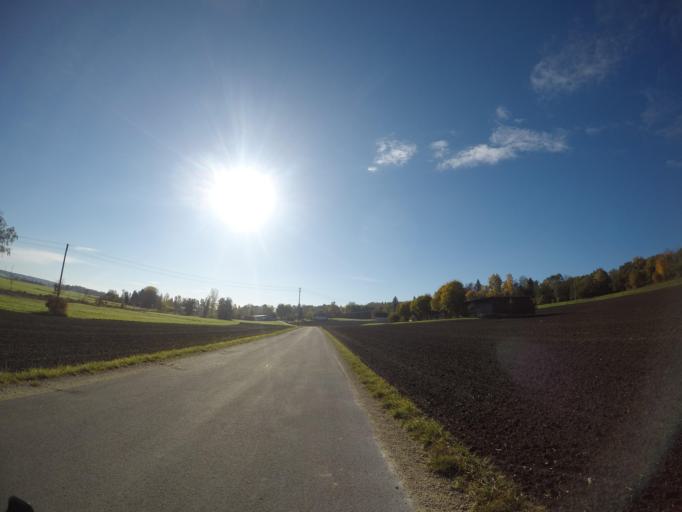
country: DE
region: Baden-Wuerttemberg
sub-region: Tuebingen Region
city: Saulgau
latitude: 48.0359
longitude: 9.4745
